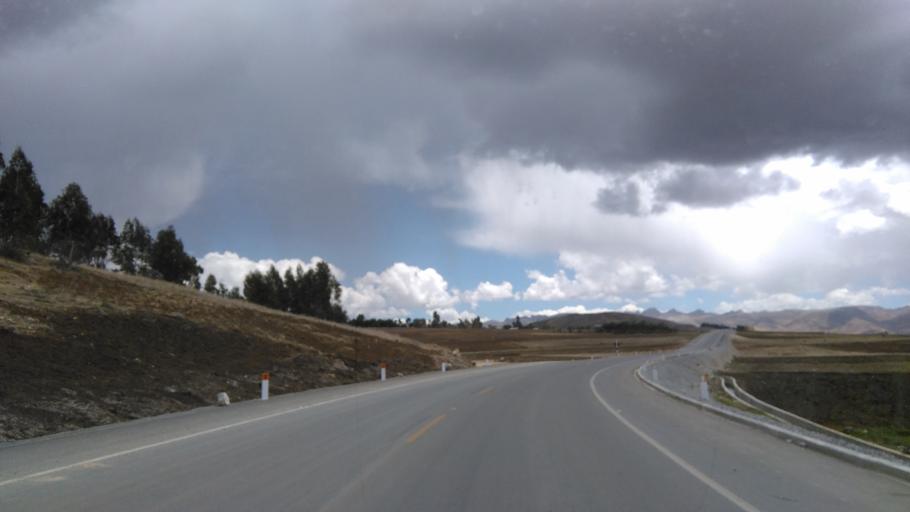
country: PE
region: Apurimac
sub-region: Provincia de Andahuaylas
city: San Jeronimo
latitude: -13.7184
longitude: -73.3494
